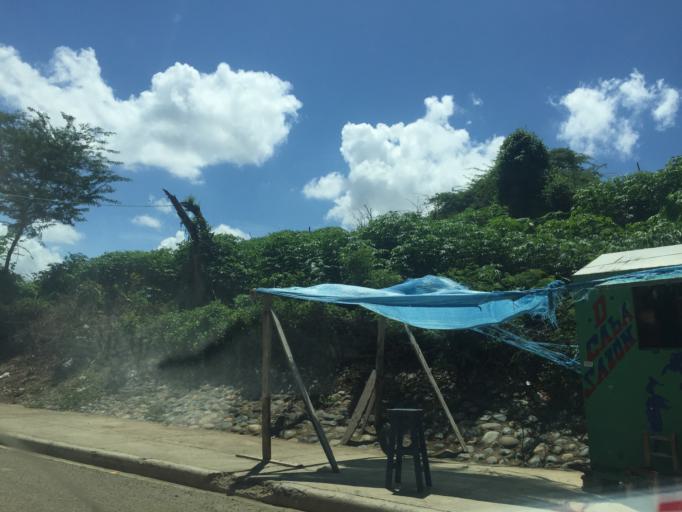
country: DO
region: Santiago
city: Santiago de los Caballeros
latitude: 19.4408
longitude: -70.7428
